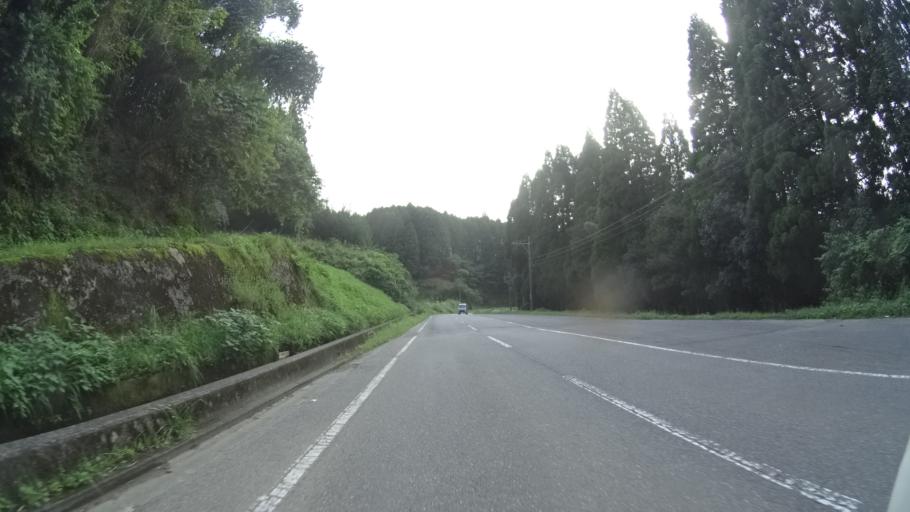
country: JP
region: Kumamoto
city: Ozu
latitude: 32.6896
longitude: 131.0128
